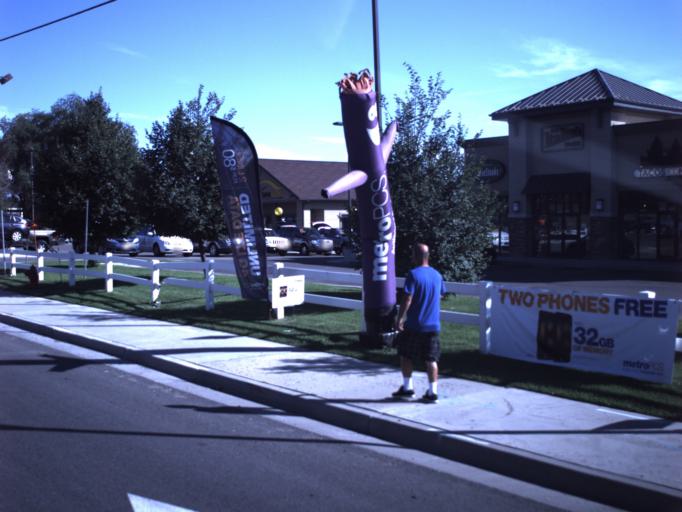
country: US
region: Utah
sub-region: Utah County
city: Lindon
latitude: 40.3488
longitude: -111.7281
